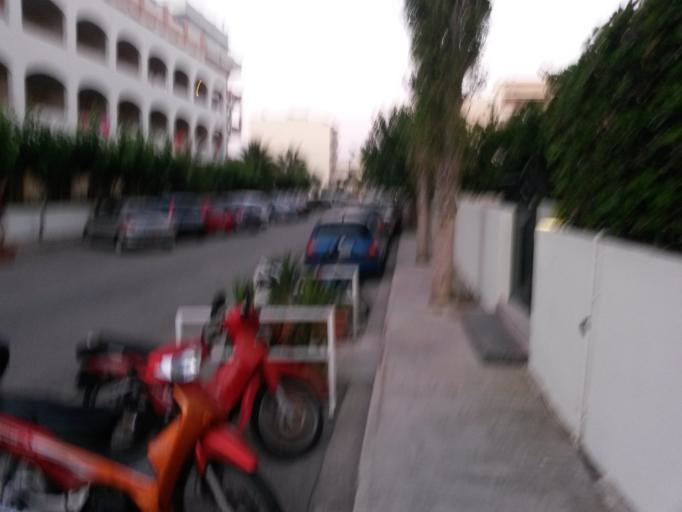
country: GR
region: Crete
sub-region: Nomos Rethymnis
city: Rethymno
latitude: 35.3656
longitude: 24.4905
